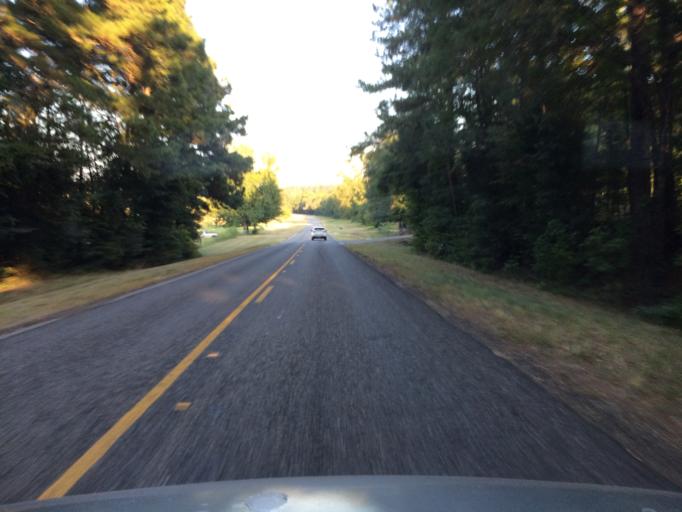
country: US
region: Texas
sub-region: Wood County
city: Hawkins
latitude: 32.7341
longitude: -95.2392
